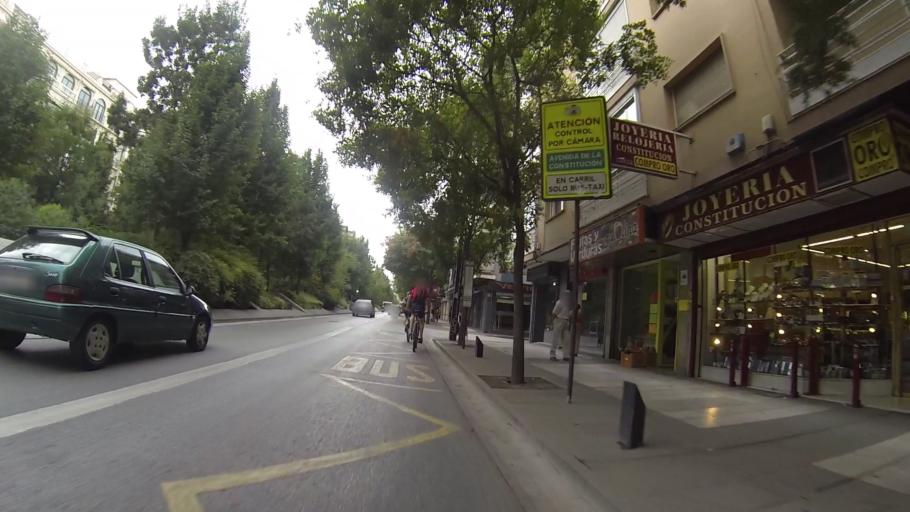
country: ES
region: Andalusia
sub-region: Provincia de Granada
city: Granada
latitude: 37.1857
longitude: -3.6079
